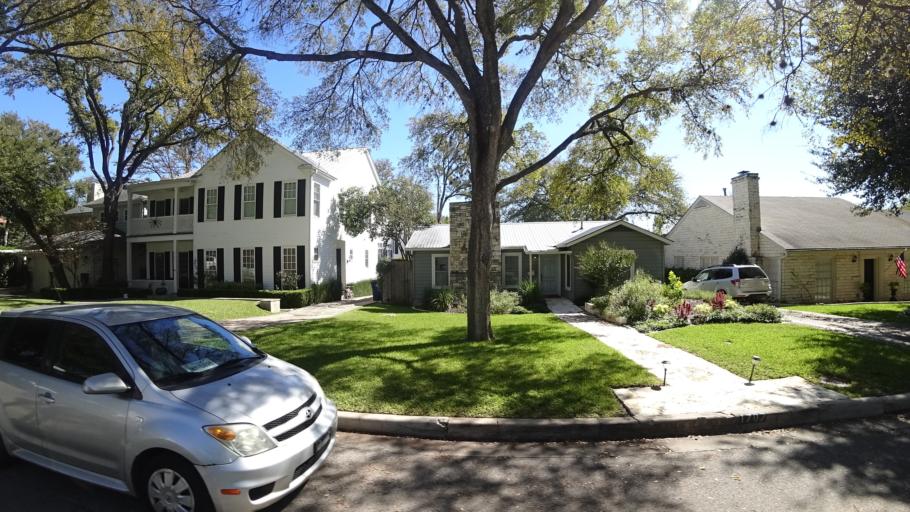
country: US
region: Texas
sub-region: Travis County
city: Rollingwood
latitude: 30.2914
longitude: -97.7662
